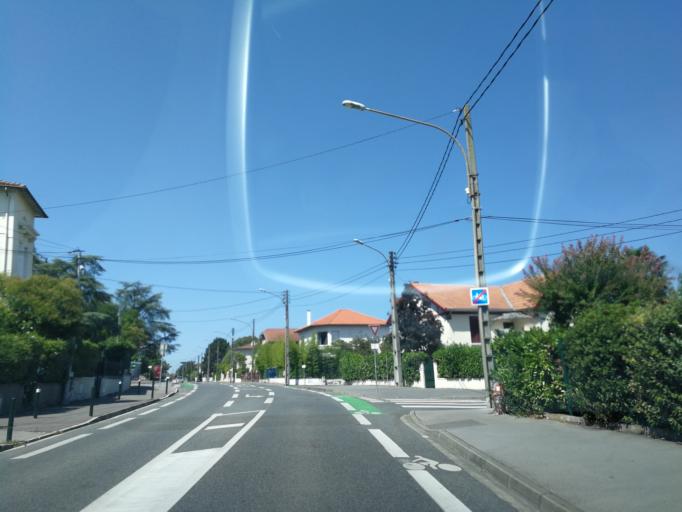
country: FR
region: Midi-Pyrenees
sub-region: Departement de la Haute-Garonne
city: Toulouse
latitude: 43.6221
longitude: 1.4689
